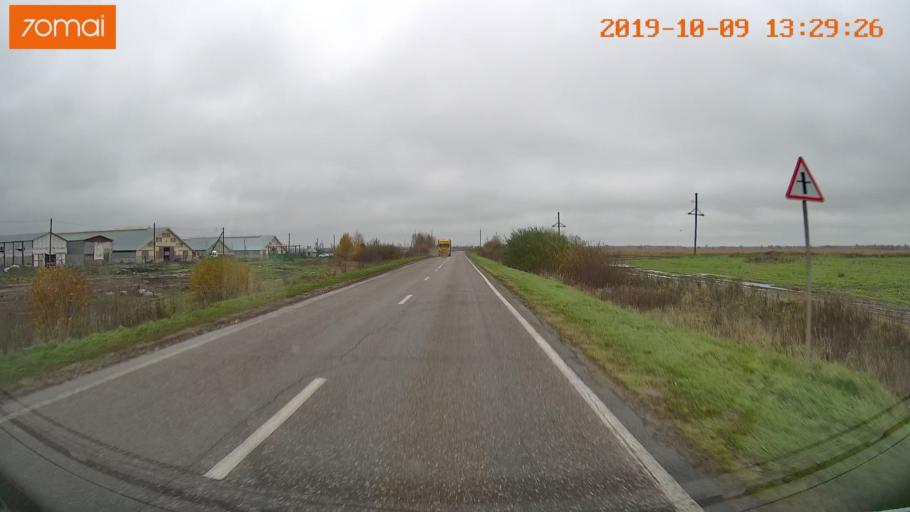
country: RU
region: Jaroslavl
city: Lyubim
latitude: 58.3160
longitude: 40.9885
